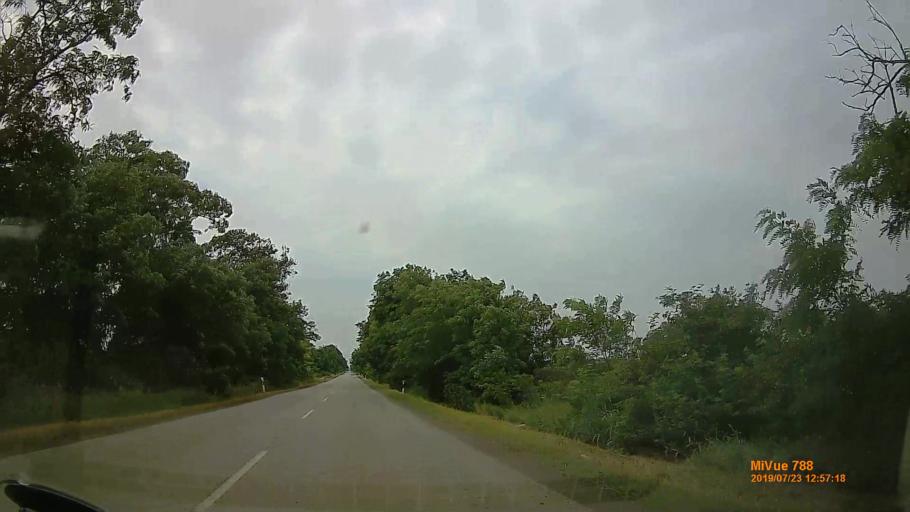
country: HU
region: Szabolcs-Szatmar-Bereg
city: Nagycserkesz
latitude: 47.9579
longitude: 21.4809
